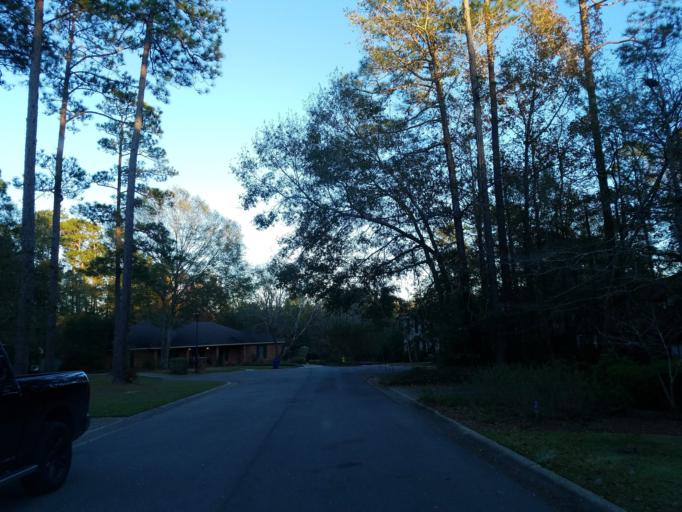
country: US
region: Mississippi
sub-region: Lamar County
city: West Hattiesburg
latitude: 31.2989
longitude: -89.3384
